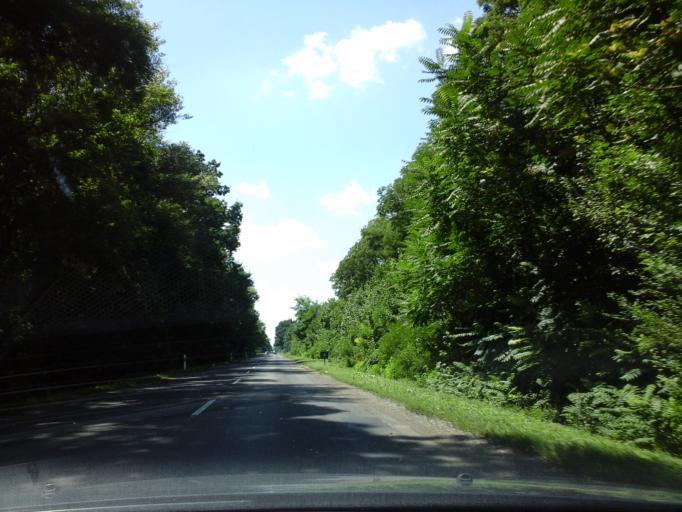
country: HU
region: Hajdu-Bihar
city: Hajduszoboszlo
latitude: 47.4587
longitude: 21.4326
